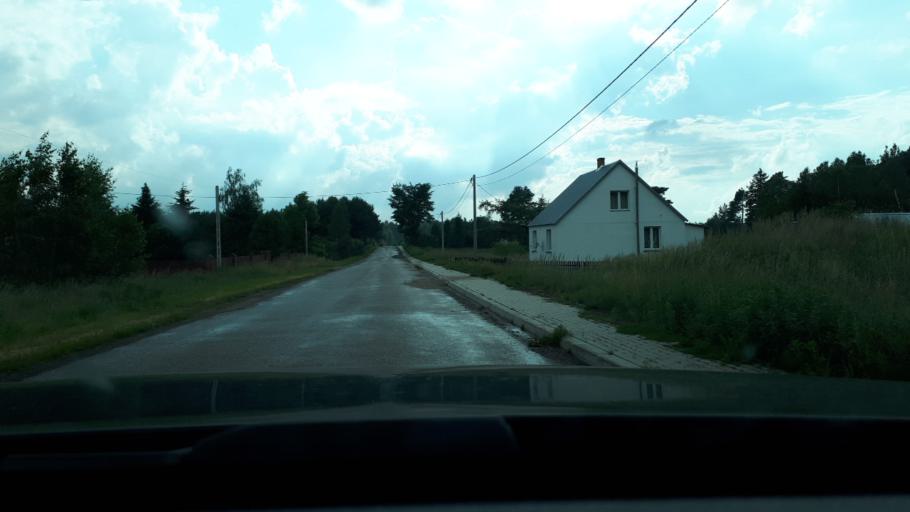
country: PL
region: Podlasie
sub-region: Powiat moniecki
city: Knyszyn
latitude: 53.2736
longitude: 22.9732
